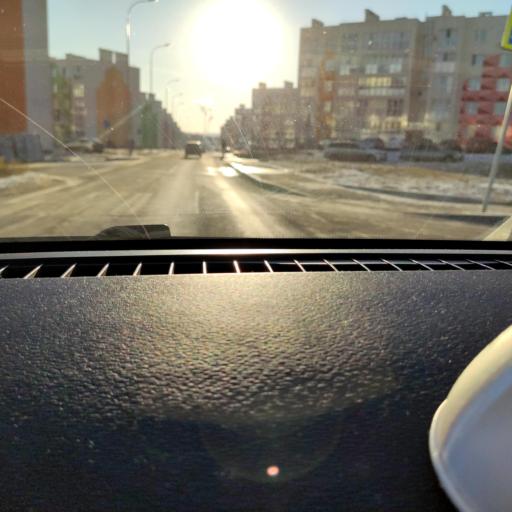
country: RU
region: Samara
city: Petra-Dubrava
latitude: 53.3033
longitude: 50.3356
